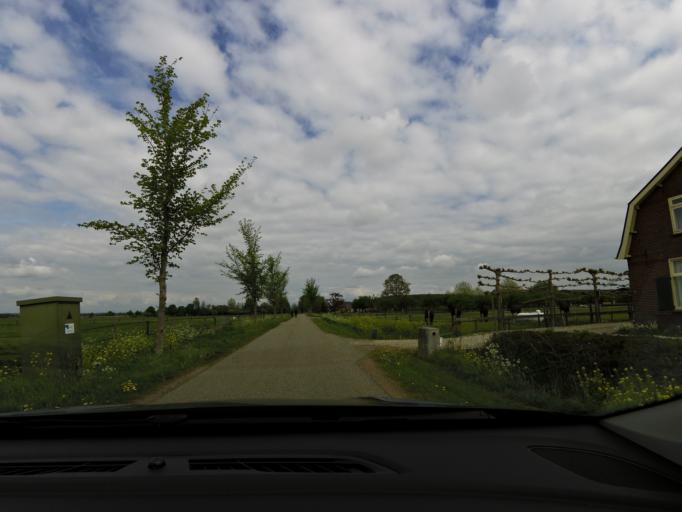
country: NL
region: Gelderland
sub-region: Gemeente Buren
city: Lienden
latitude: 51.9351
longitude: 5.4701
